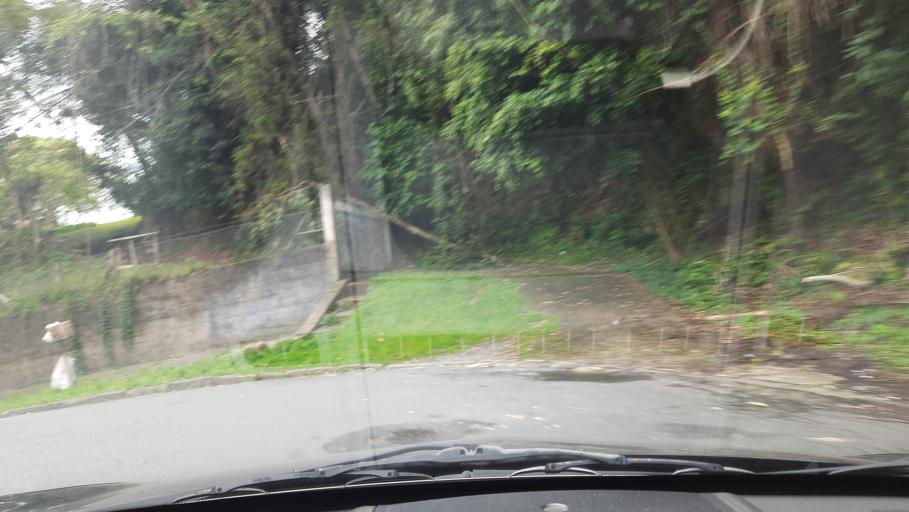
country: BR
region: Minas Gerais
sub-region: Pocos De Caldas
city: Pocos de Caldas
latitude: -21.7791
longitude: -46.5663
